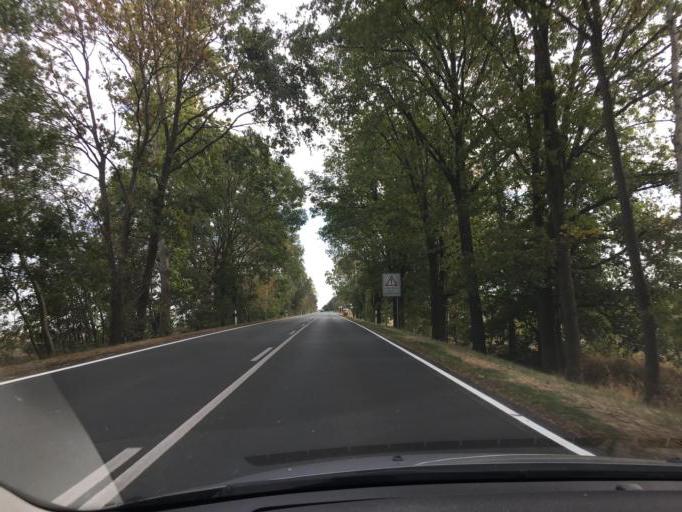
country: DE
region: Saxony
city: Oschatz
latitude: 51.2839
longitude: 13.1611
